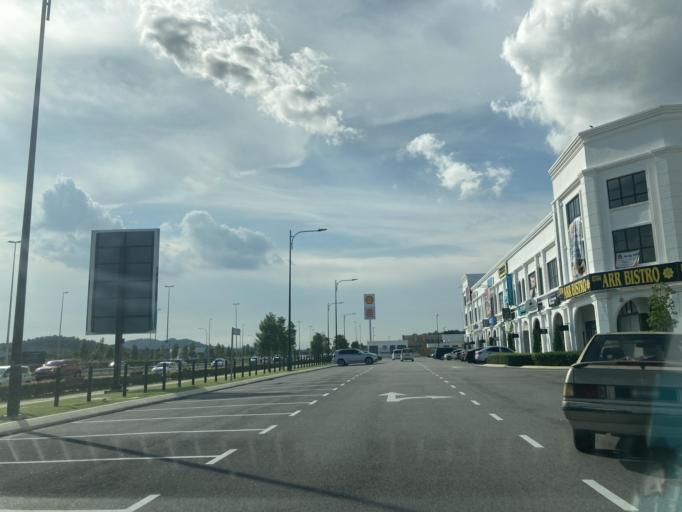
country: MY
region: Selangor
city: Batu Arang
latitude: 3.2320
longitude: 101.4508
